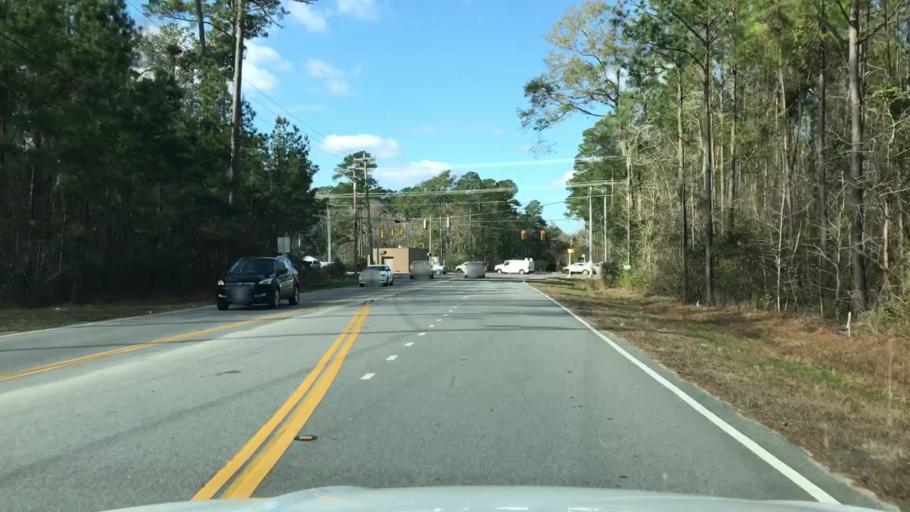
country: US
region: South Carolina
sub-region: Horry County
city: Socastee
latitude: 33.6600
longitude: -79.0115
